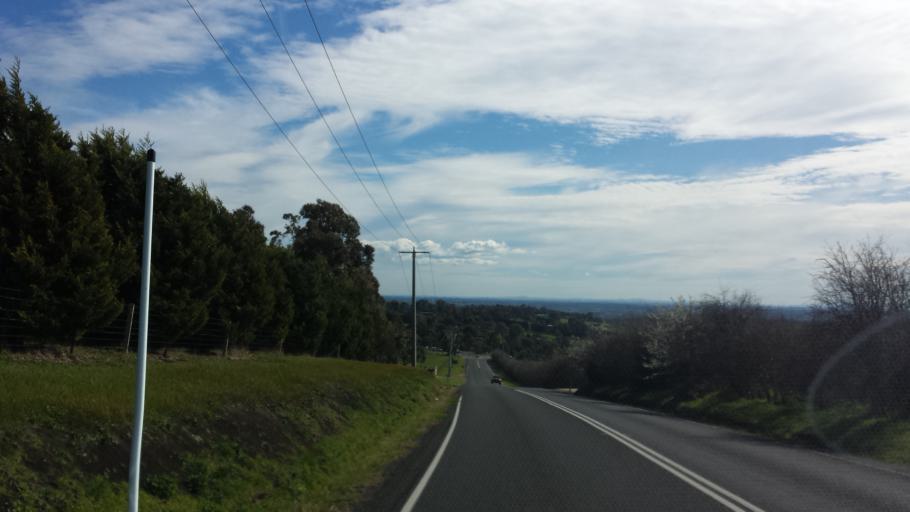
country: AU
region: Victoria
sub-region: Nillumbik
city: North Warrandyte
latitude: -37.6959
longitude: 145.2196
